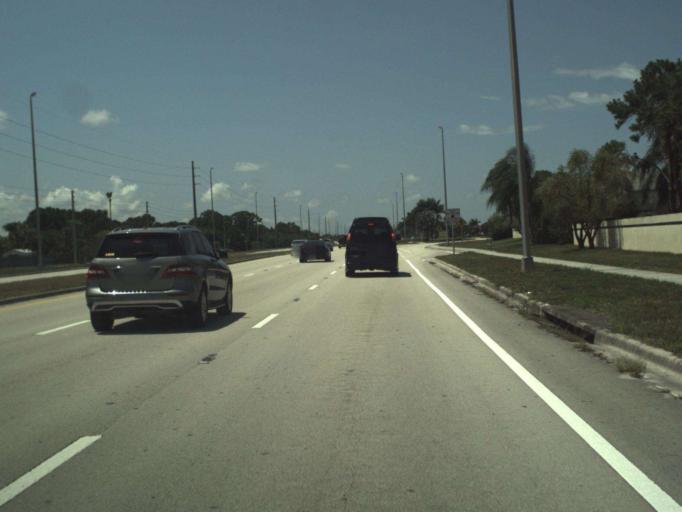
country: US
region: Florida
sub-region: Saint Lucie County
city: Port Saint Lucie
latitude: 27.2909
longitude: -80.2997
